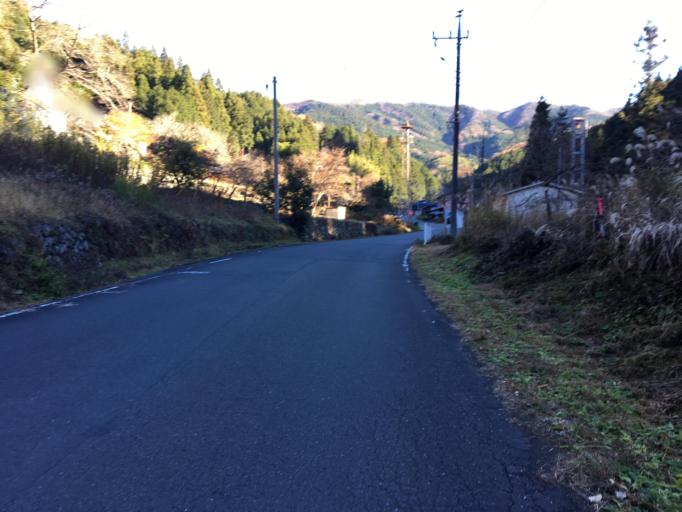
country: JP
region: Saitama
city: Chichibu
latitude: 36.0190
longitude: 139.1708
